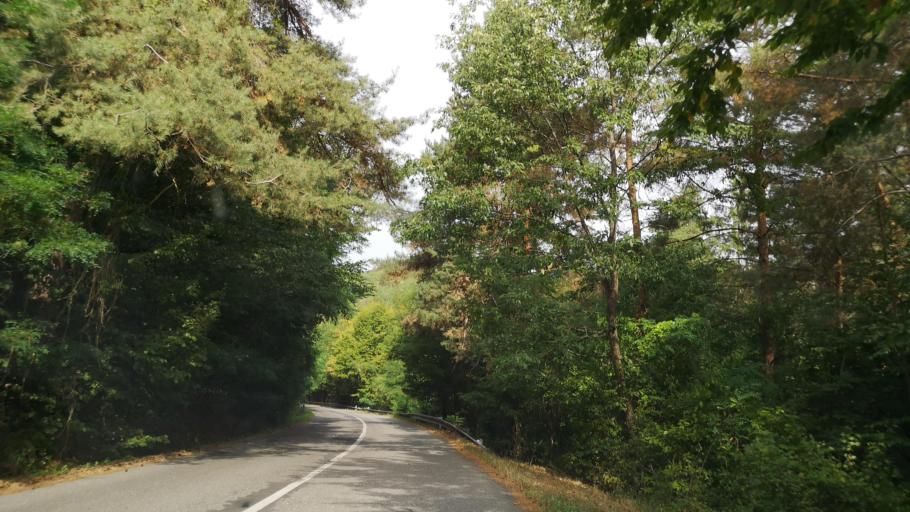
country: SK
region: Banskobystricky
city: Revuca
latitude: 48.5835
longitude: 20.0800
